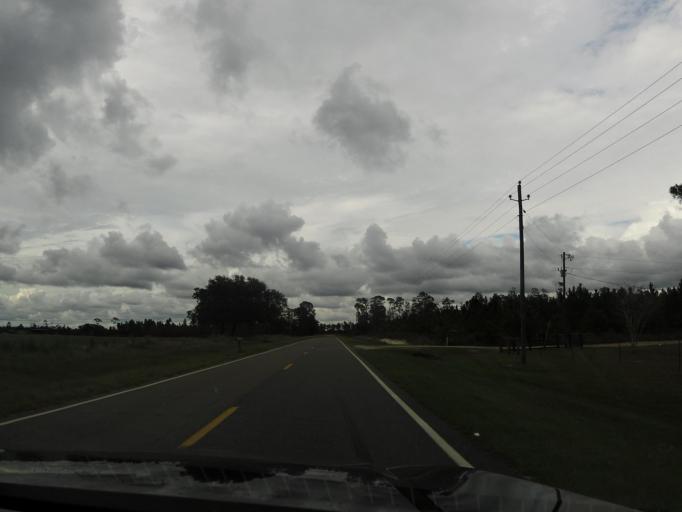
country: US
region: Florida
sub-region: Baker County
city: Macclenny
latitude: 30.4249
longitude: -82.1992
